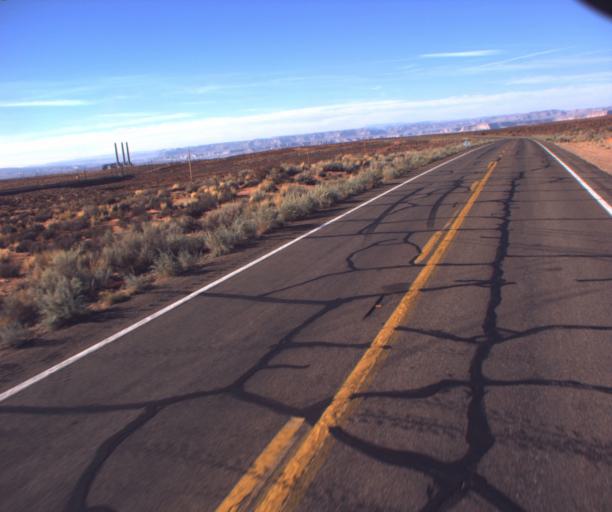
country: US
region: Arizona
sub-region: Coconino County
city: LeChee
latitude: 36.8741
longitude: -111.3427
